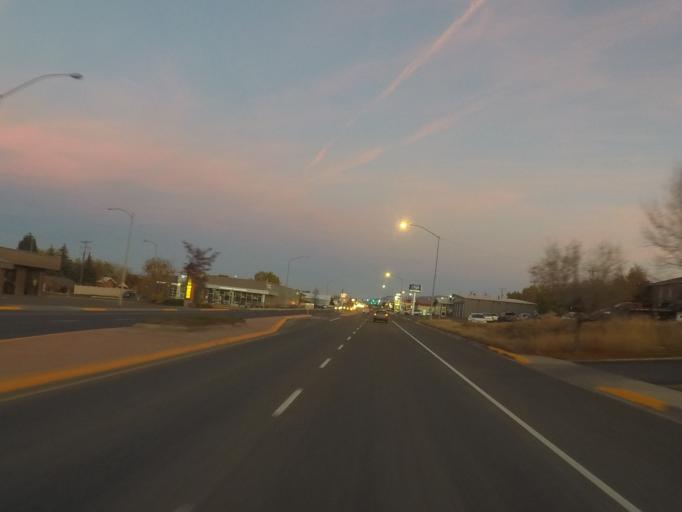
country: US
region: Montana
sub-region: Lewis and Clark County
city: Helena
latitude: 46.6046
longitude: -112.0616
